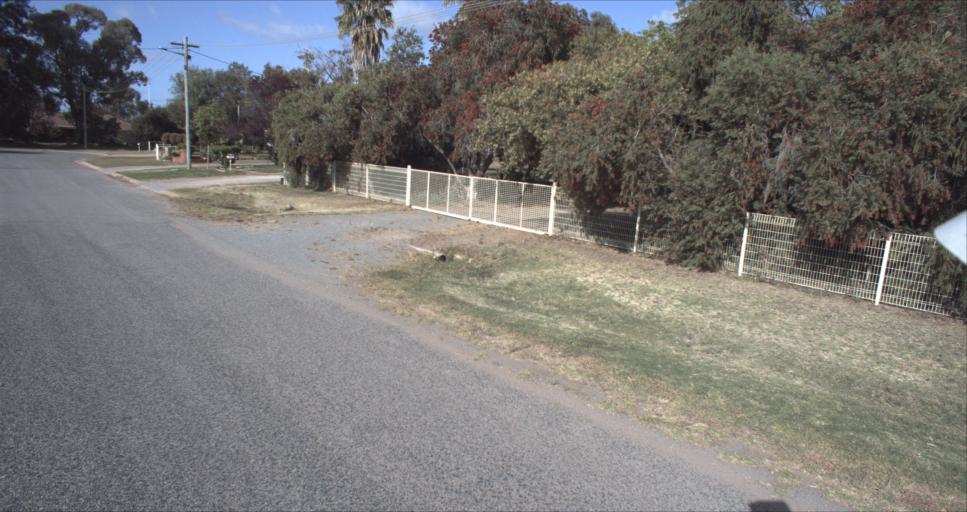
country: AU
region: New South Wales
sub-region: Leeton
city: Leeton
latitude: -34.5692
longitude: 146.3919
